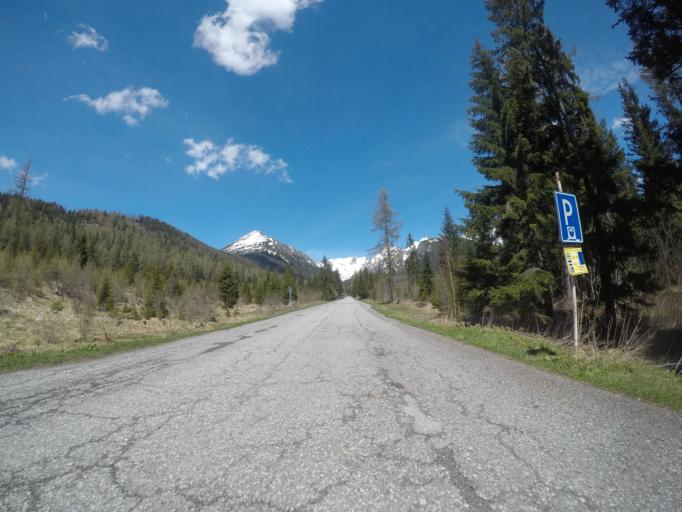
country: SK
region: Presovsky
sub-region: Okres Poprad
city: Strba
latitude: 49.1216
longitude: 20.0748
